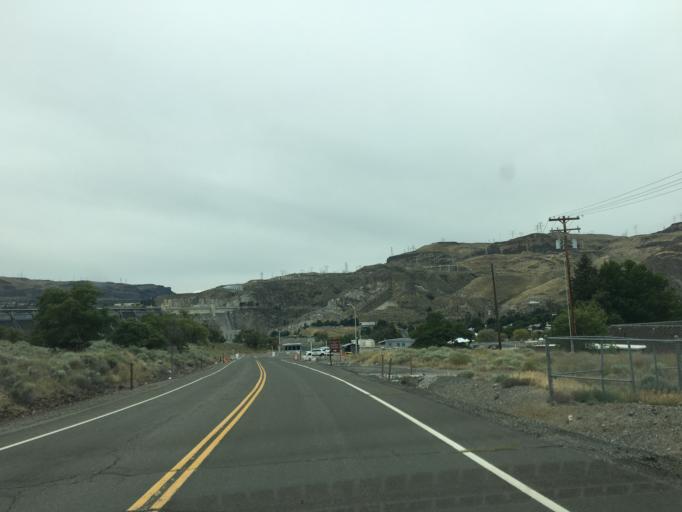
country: US
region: Washington
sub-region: Okanogan County
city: Coulee Dam
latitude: 47.9665
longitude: -118.9721
